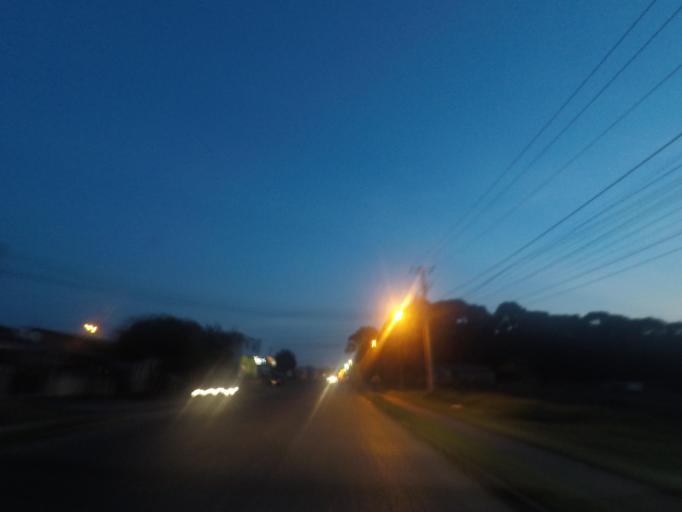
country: BR
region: Parana
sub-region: Pinhais
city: Pinhais
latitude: -25.4777
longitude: -49.1512
